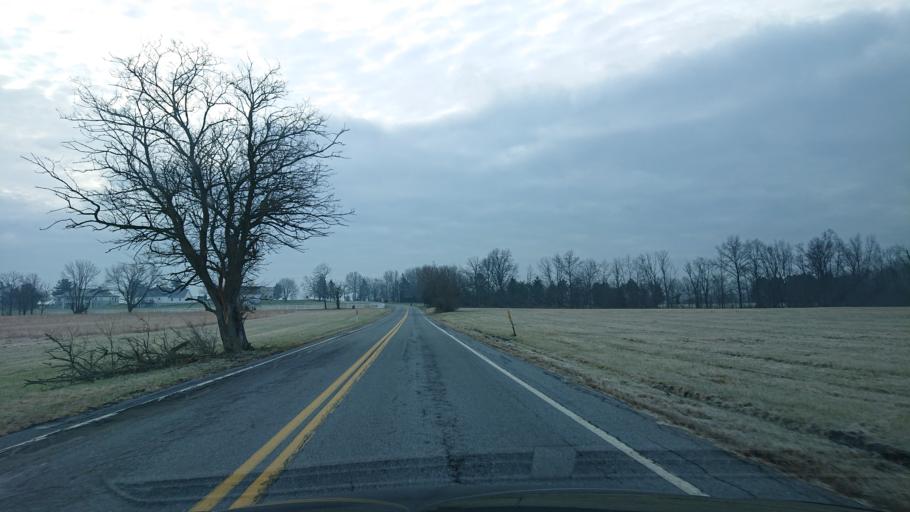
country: US
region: Pennsylvania
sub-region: Lebanon County
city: Palmyra
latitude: 40.4152
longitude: -76.6064
